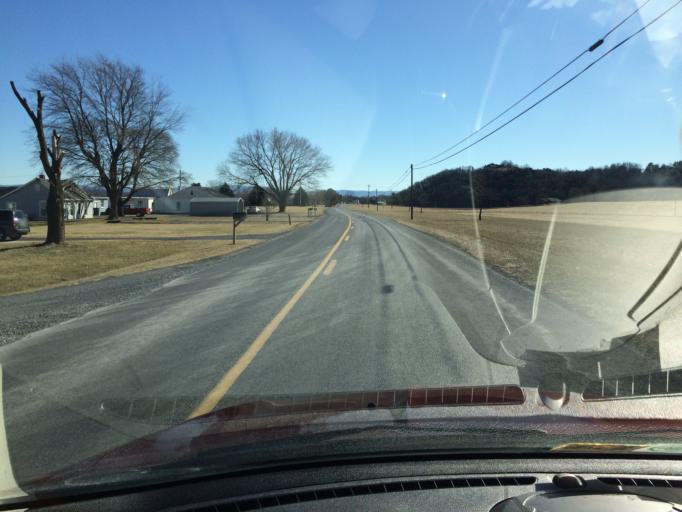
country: US
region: Virginia
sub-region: Rockingham County
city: Bridgewater
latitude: 38.3623
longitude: -78.9606
